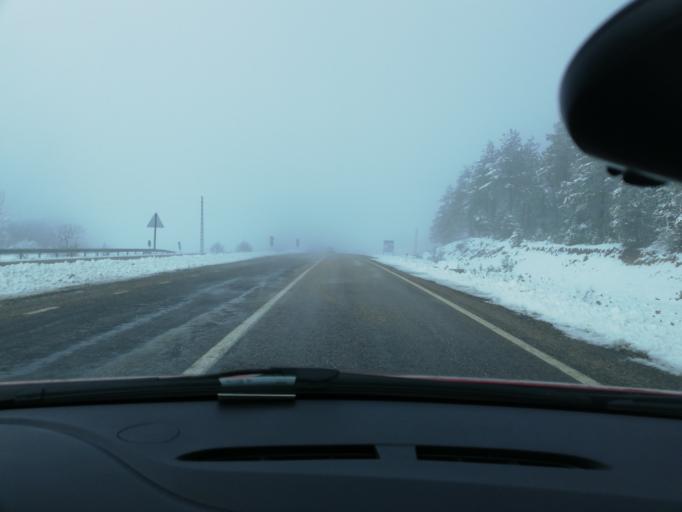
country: TR
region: Kastamonu
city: Akkaya
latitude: 41.2990
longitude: 33.5246
